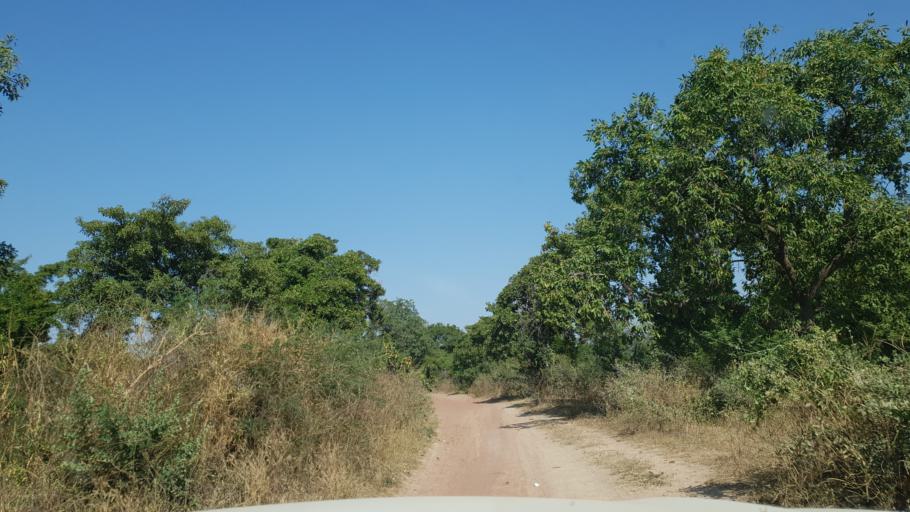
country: ML
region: Sikasso
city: Yorosso
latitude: 12.2683
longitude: -4.6988
